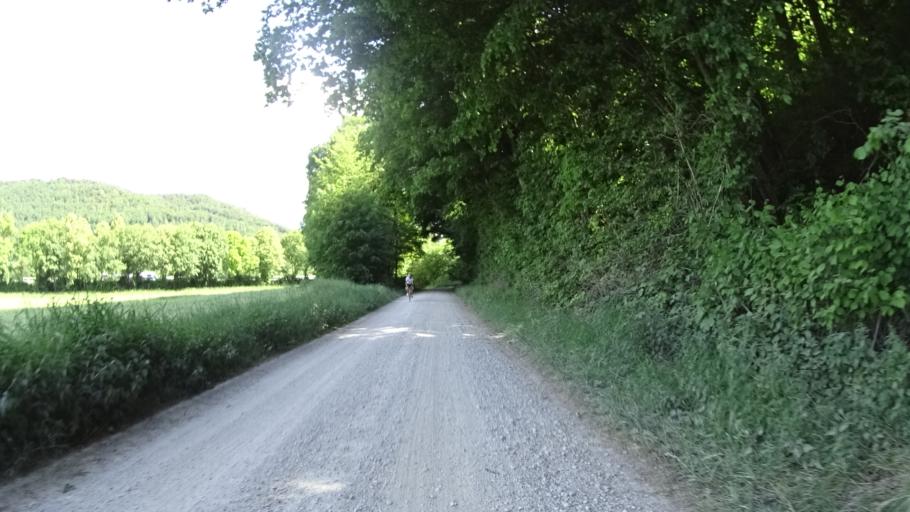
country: DE
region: Bavaria
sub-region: Regierungsbezirk Mittelfranken
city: Greding
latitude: 49.0153
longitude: 11.3557
